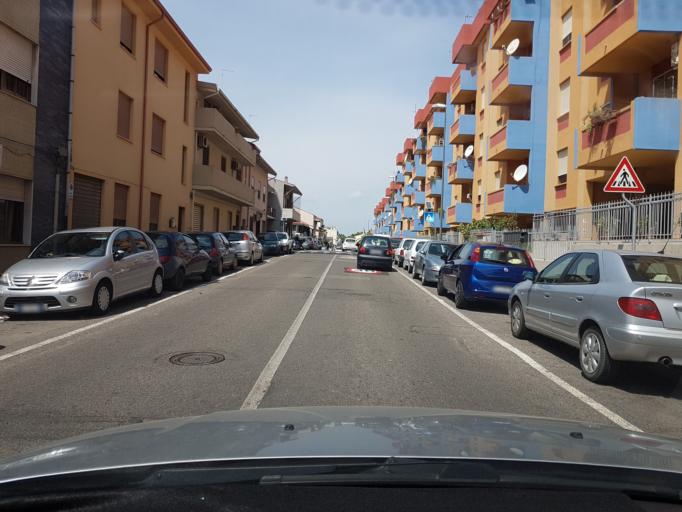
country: IT
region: Sardinia
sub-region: Provincia di Oristano
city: Oristano
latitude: 39.9095
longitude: 8.5995
